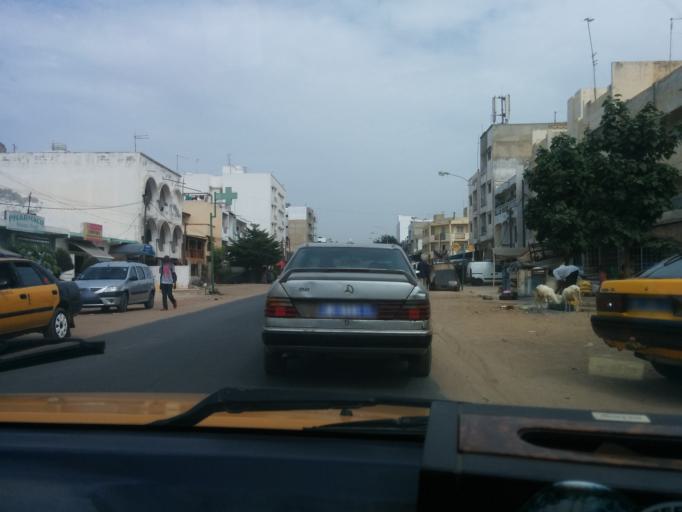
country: SN
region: Dakar
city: Grand Dakar
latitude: 14.7559
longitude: -17.4443
